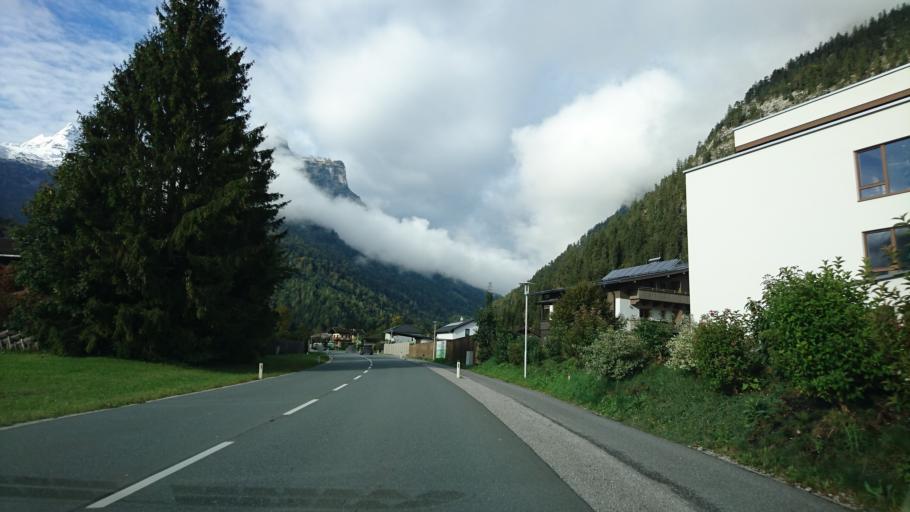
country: AT
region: Salzburg
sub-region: Politischer Bezirk Zell am See
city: Lofer
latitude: 47.5828
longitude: 12.6903
